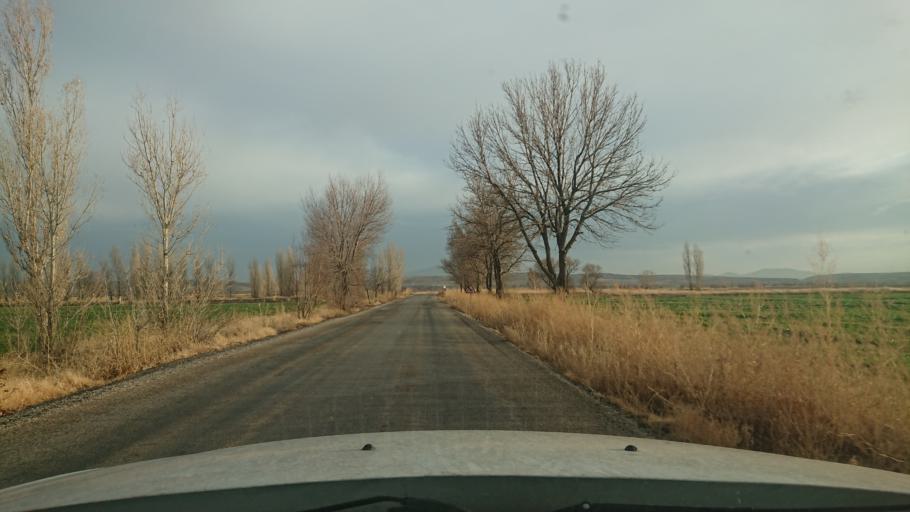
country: TR
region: Aksaray
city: Acipinar
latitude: 38.4707
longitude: 33.8507
